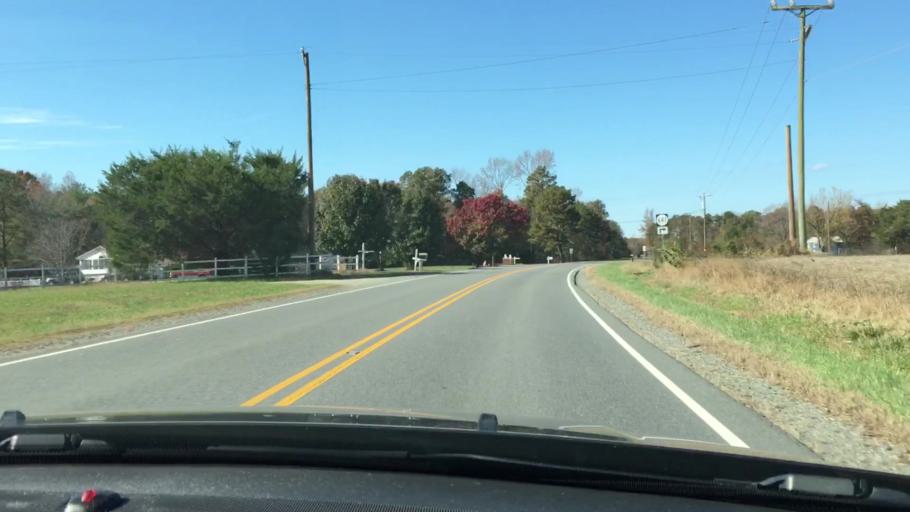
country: US
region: Virginia
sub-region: King William County
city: King William
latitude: 37.6602
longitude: -76.9586
